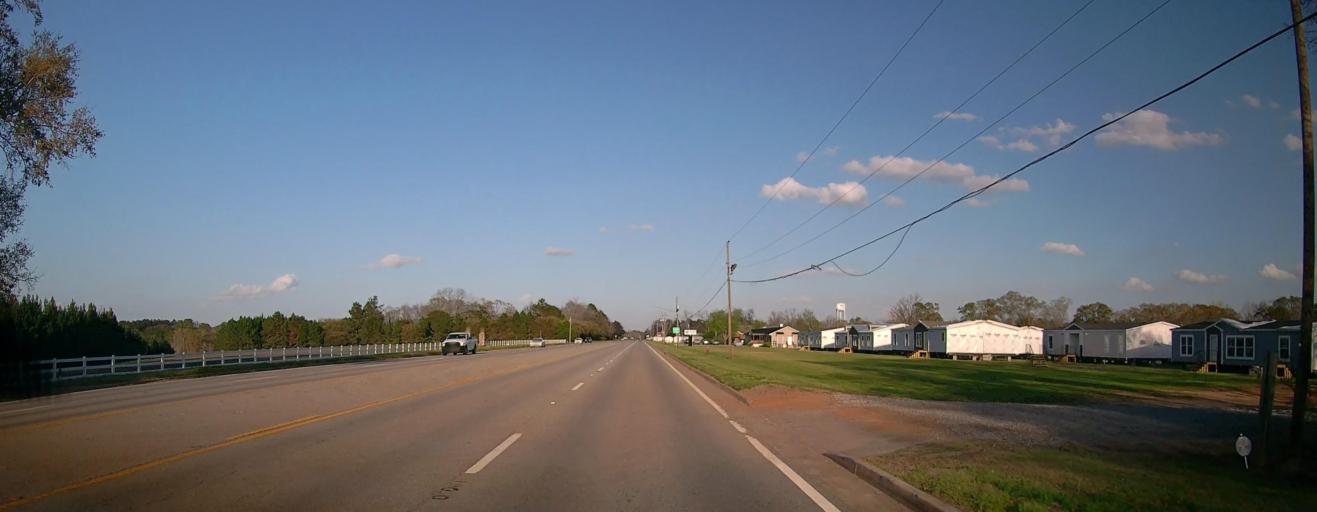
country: US
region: Georgia
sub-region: Evans County
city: Claxton
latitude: 32.1563
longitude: -81.9424
